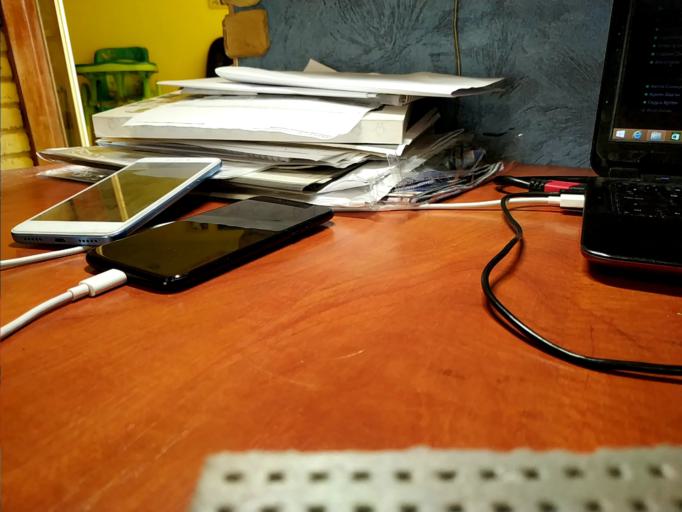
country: RU
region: Tverskaya
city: Spirovo
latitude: 57.4318
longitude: 35.0388
